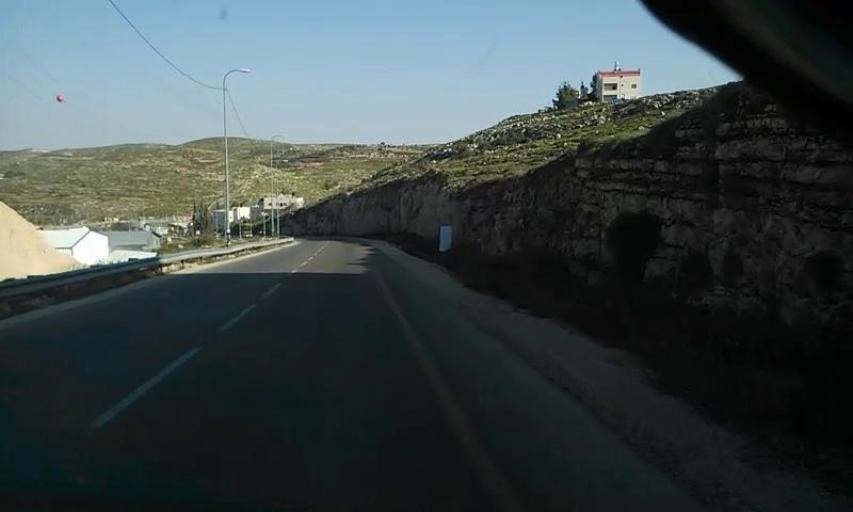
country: PS
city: Khallat ad Dar
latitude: 31.5009
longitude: 35.1169
